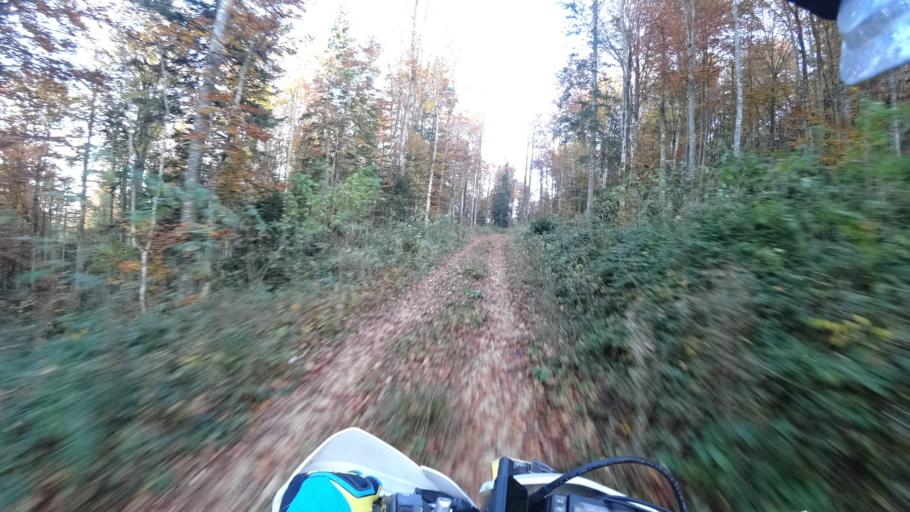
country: HR
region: Karlovacka
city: Plaski
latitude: 44.9641
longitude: 15.3960
